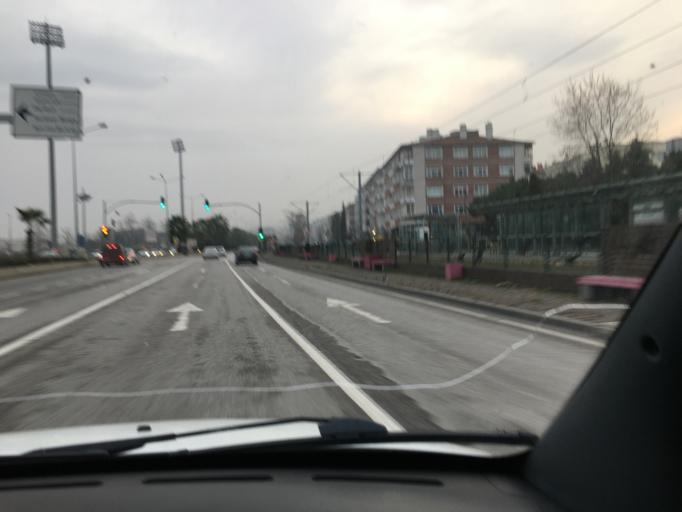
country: TR
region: Samsun
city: Samsun
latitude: 41.3106
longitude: 36.3357
